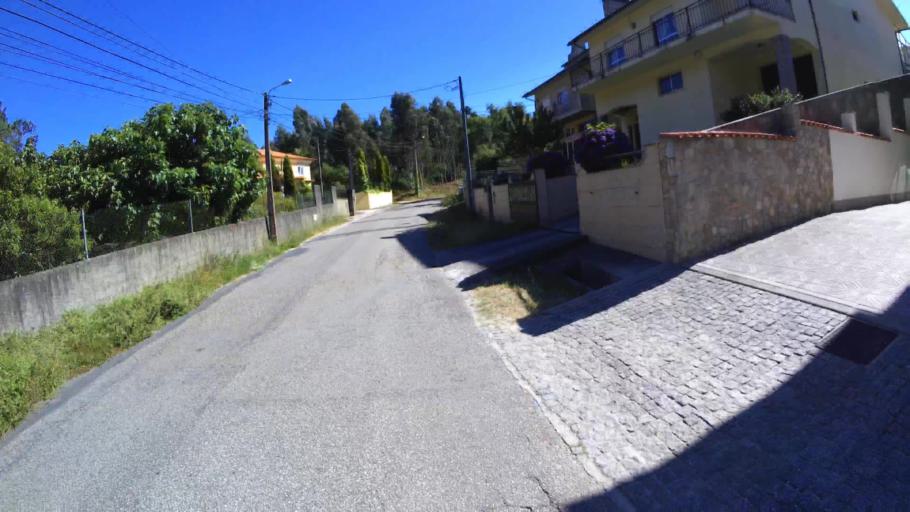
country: PT
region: Aveiro
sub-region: Aveiro
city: Aveiro
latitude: 40.6628
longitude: -8.6206
